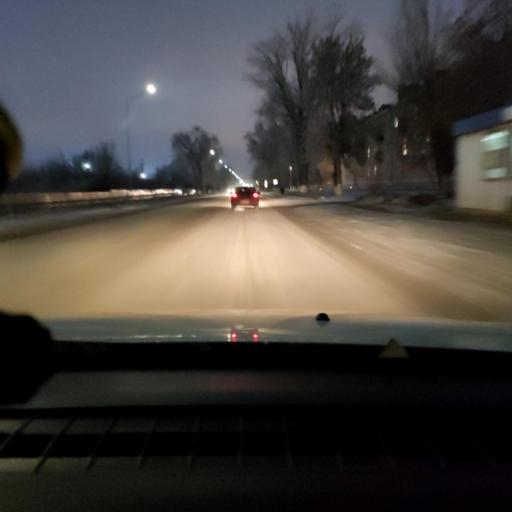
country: RU
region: Samara
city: Chapayevsk
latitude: 52.9717
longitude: 49.6996
